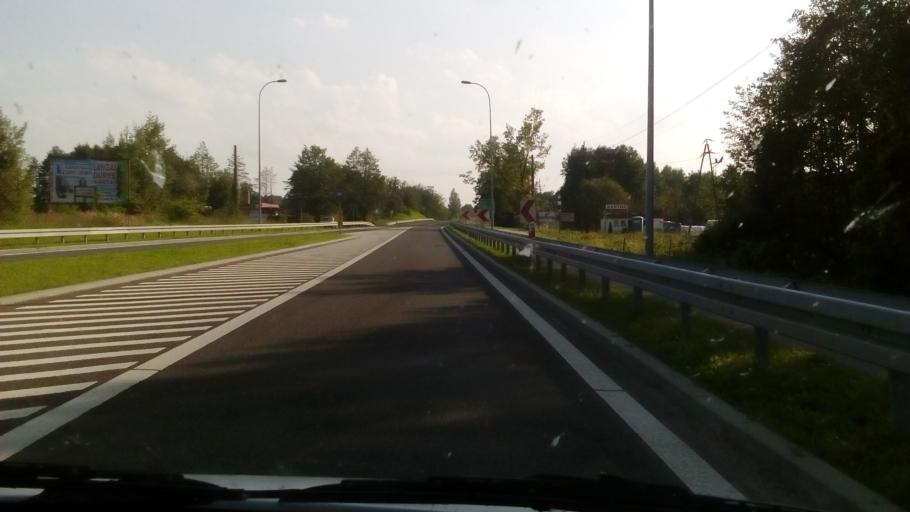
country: LT
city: Lazdijai
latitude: 54.1575
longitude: 23.4726
